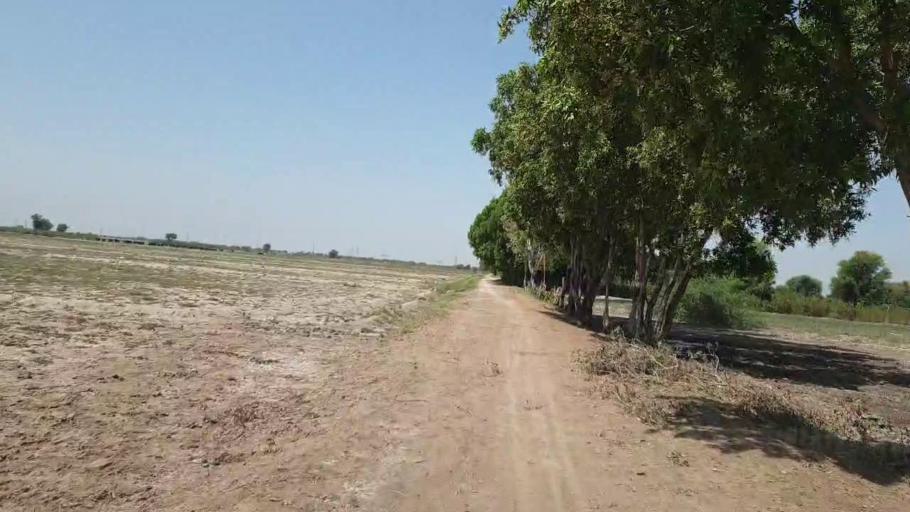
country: PK
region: Sindh
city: Hyderabad
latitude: 25.4718
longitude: 68.4244
